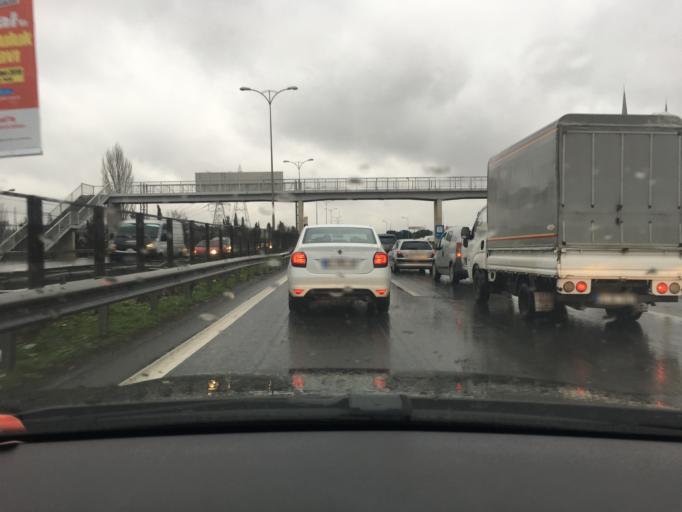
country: TR
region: Istanbul
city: Esenler
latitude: 41.0489
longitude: 28.8851
